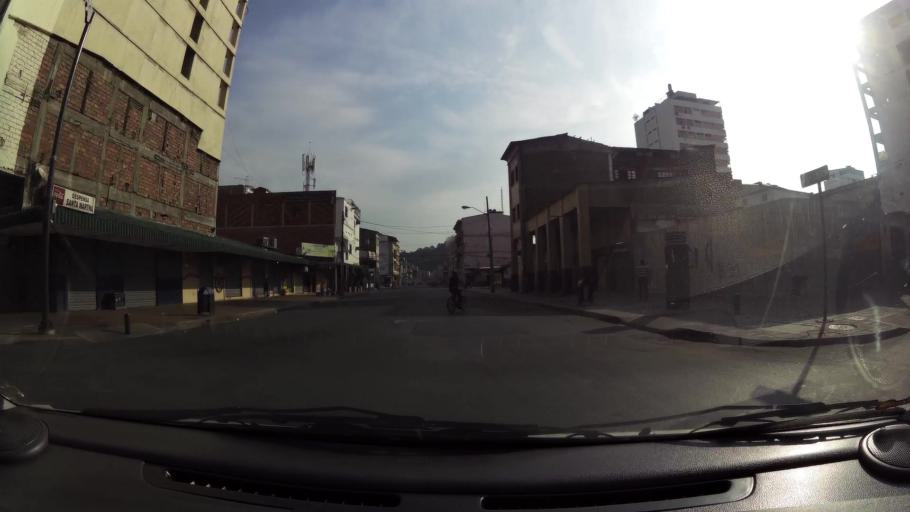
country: EC
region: Guayas
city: Guayaquil
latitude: -2.1892
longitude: -79.8859
